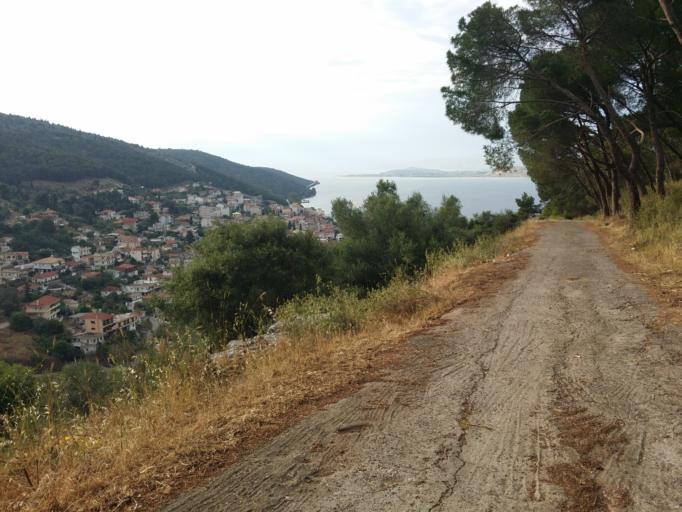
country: GR
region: West Greece
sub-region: Nomos Aitolias kai Akarnanias
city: Amfilochia
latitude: 38.8573
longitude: 21.1668
